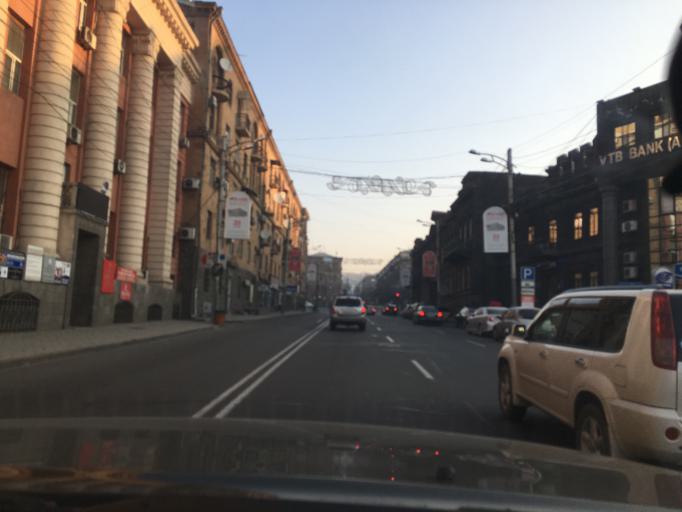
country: AM
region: Yerevan
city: Yerevan
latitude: 40.1789
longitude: 44.5155
